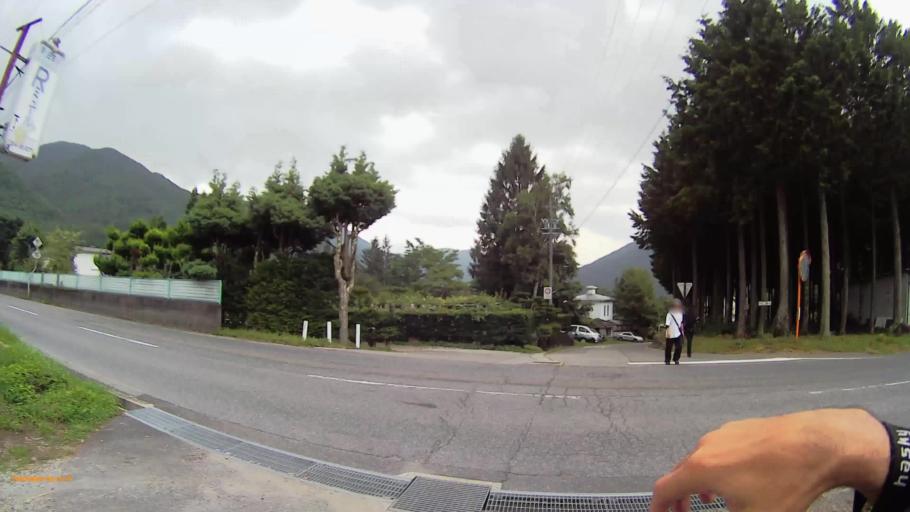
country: JP
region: Nagano
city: Ina
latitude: 35.9437
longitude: 137.7873
